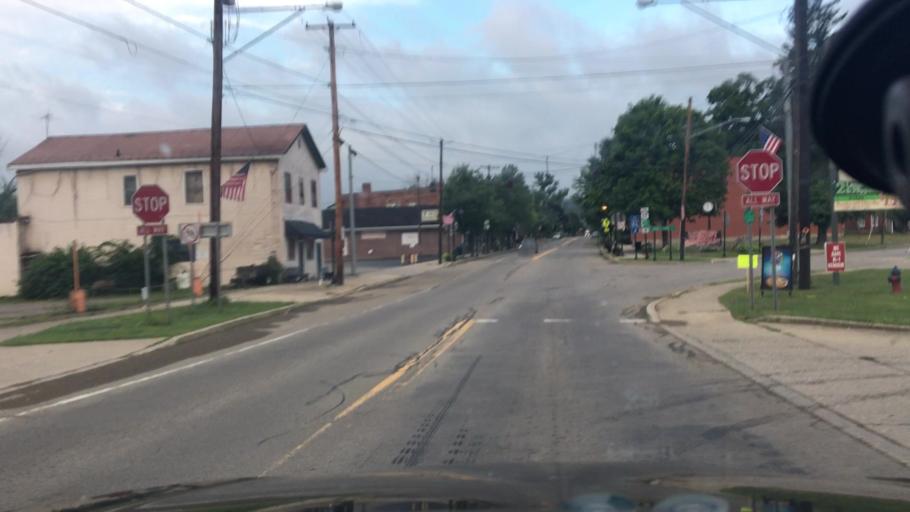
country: US
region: New York
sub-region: Cattaraugus County
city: Randolph
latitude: 42.1623
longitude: -78.9749
